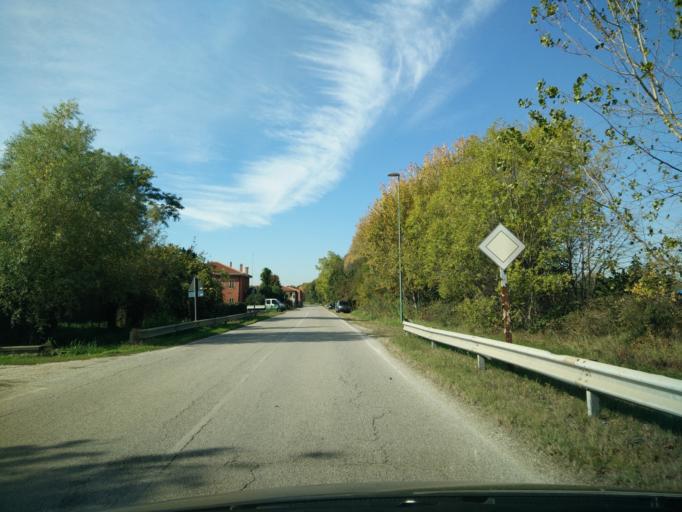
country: IT
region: Veneto
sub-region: Provincia di Venezia
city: Mestre
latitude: 45.4280
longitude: 12.2400
